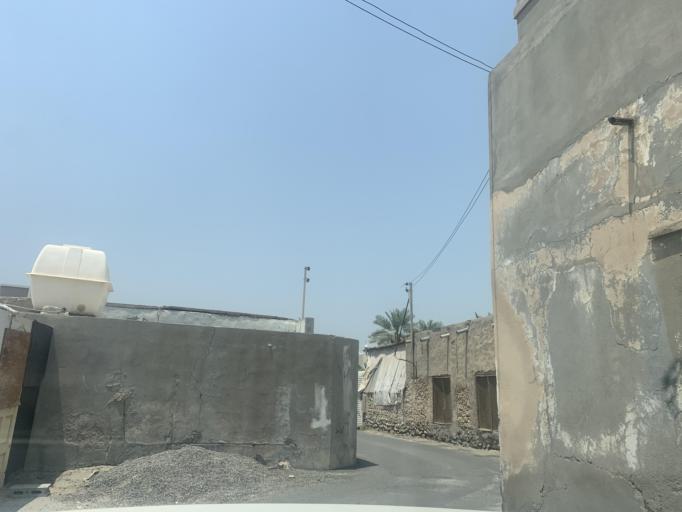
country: BH
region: Central Governorate
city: Madinat Hamad
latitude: 26.1434
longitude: 50.4593
